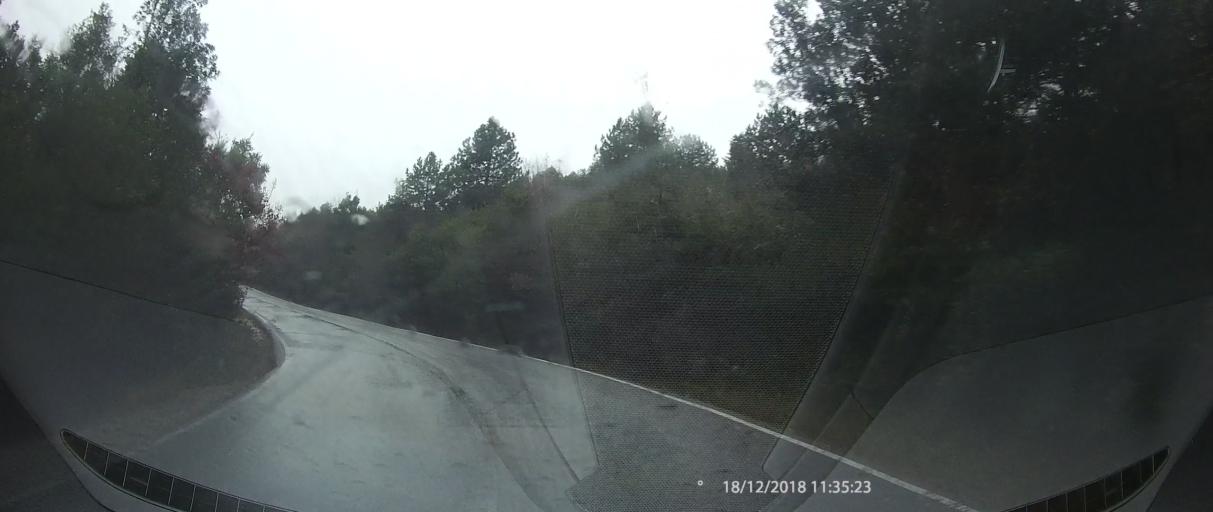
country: GR
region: Central Macedonia
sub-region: Nomos Pierias
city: Litochoro
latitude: 40.1155
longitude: 22.4860
